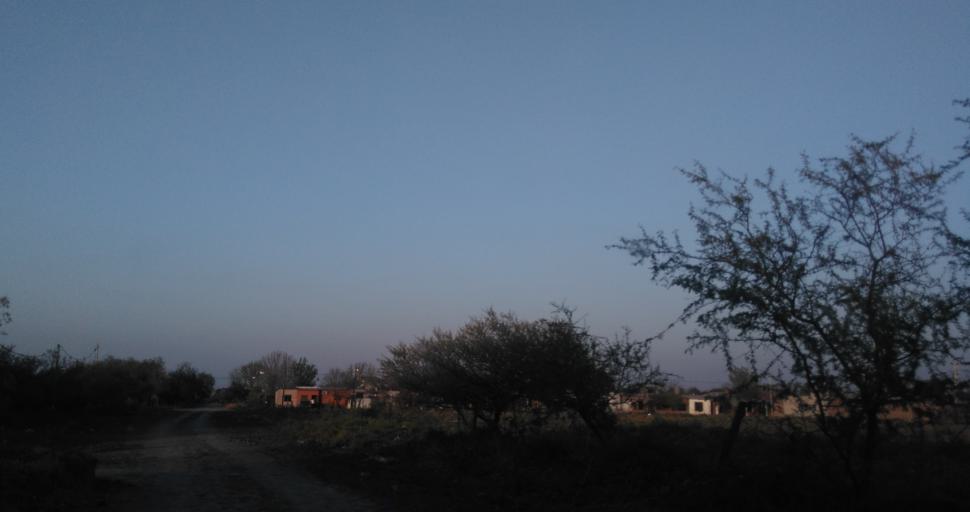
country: AR
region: Chaco
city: Resistencia
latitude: -27.4816
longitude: -59.0028
